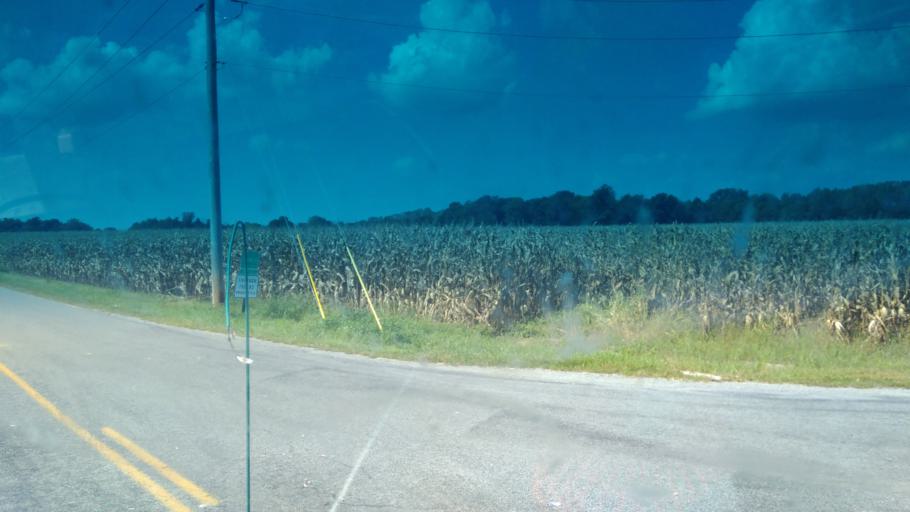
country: US
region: Ohio
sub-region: Hardin County
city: Ada
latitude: 40.7033
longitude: -83.8802
